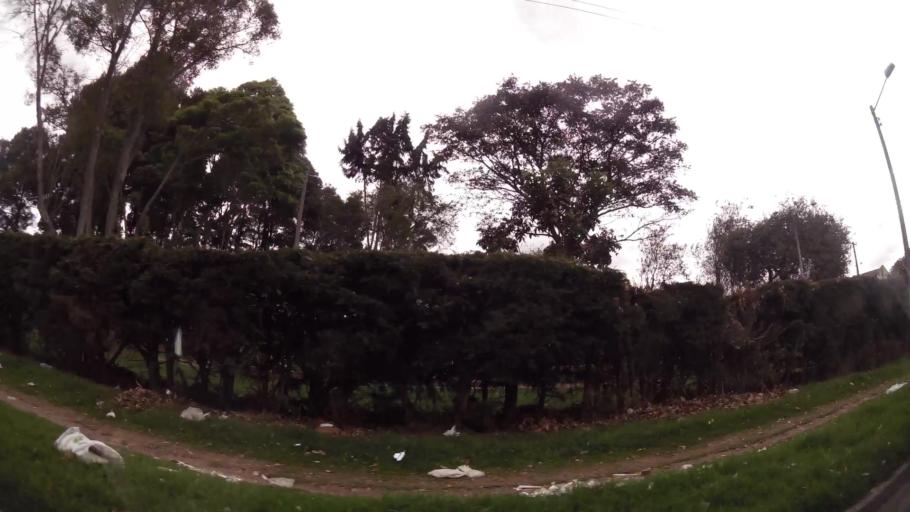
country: CO
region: Cundinamarca
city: Funza
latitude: 4.7191
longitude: -74.1242
